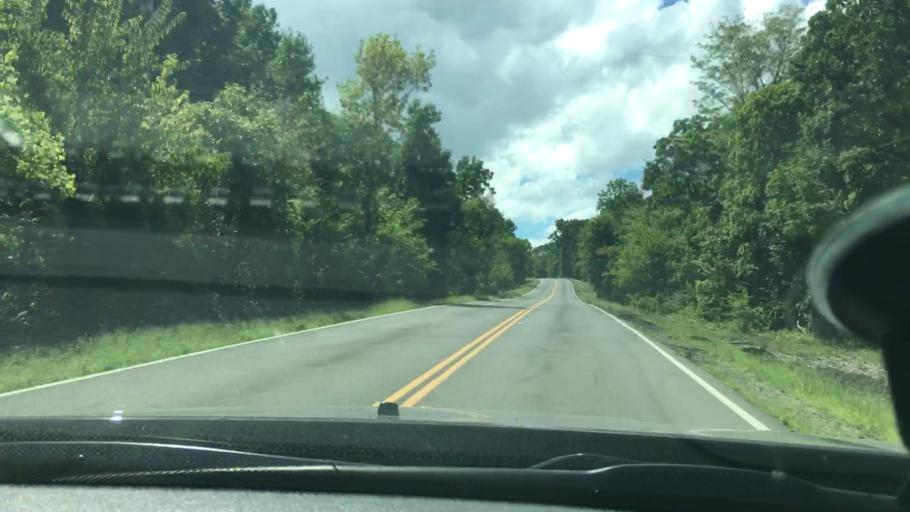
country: US
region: Oklahoma
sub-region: Sequoyah County
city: Vian
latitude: 35.6655
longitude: -94.9419
